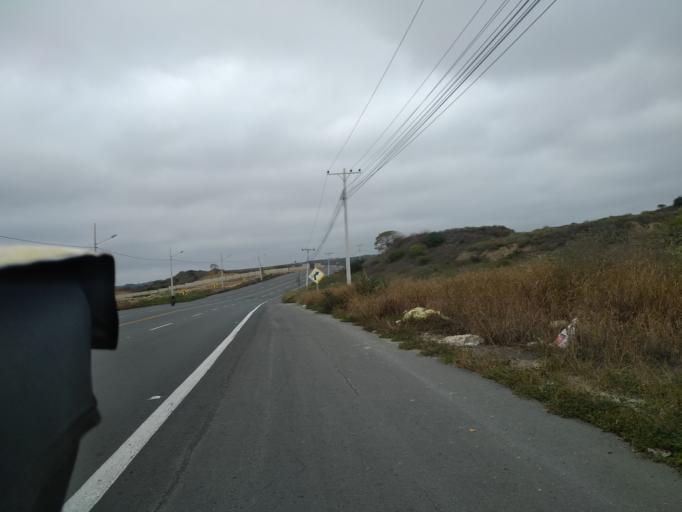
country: EC
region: Santa Elena
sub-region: Canton Santa Elena
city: Santa Elena
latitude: -2.2004
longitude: -80.8546
